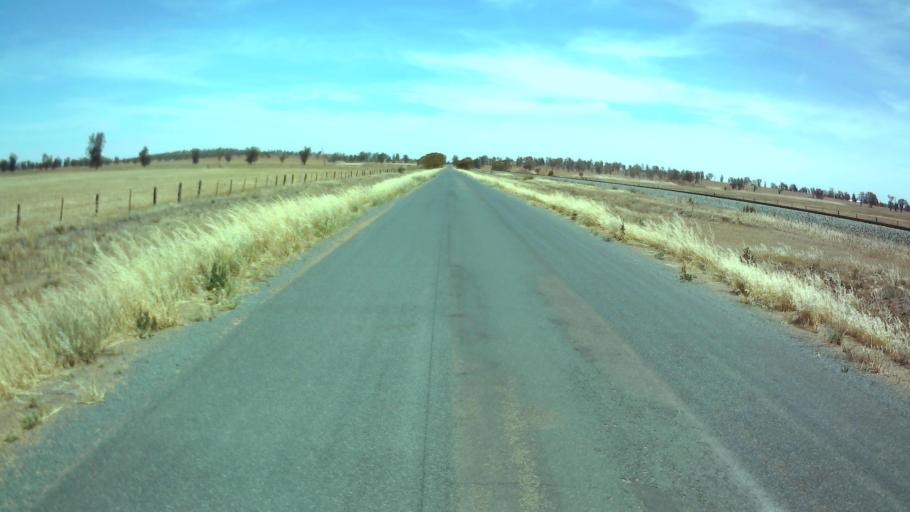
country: AU
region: New South Wales
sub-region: Weddin
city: Grenfell
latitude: -33.7595
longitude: 147.7614
